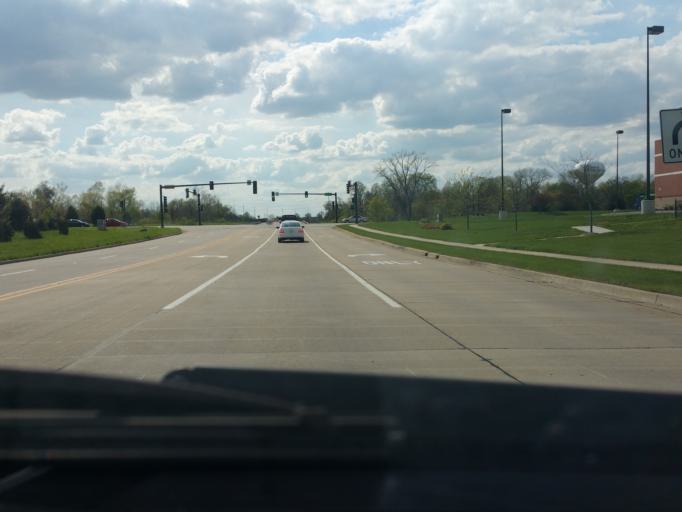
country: US
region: Illinois
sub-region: Madison County
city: Edwardsville
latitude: 38.7873
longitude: -89.9554
